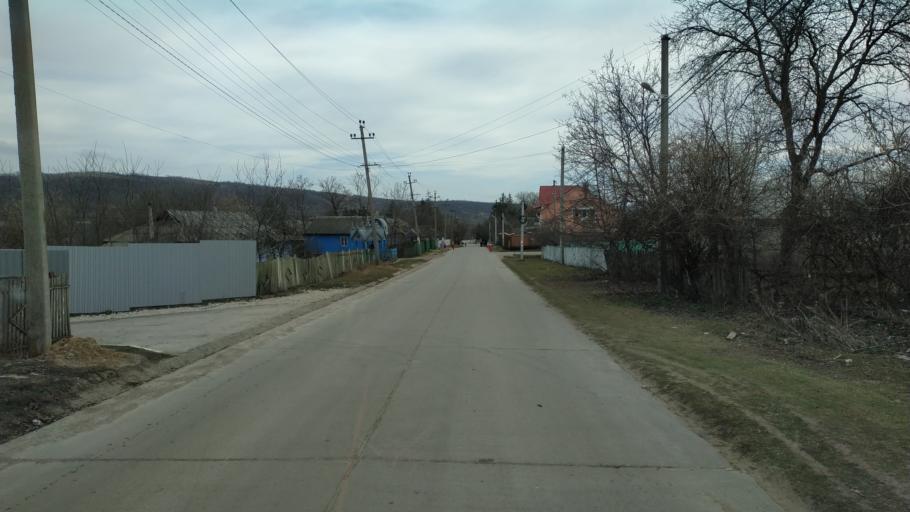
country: MD
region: Hincesti
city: Dancu
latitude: 46.9253
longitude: 28.2642
